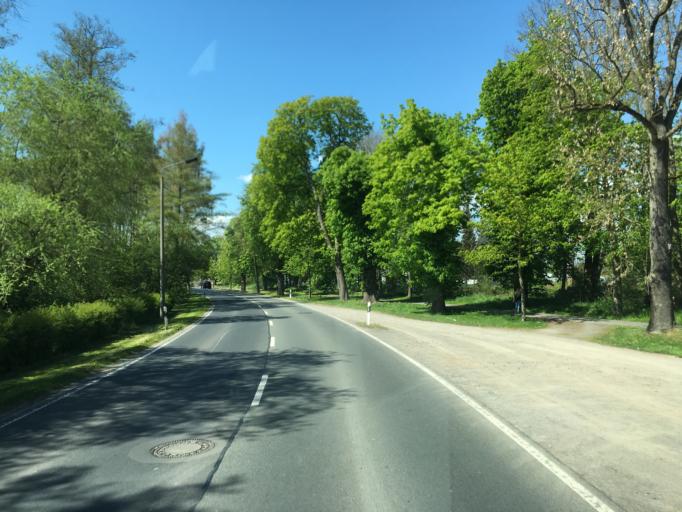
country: DE
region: Thuringia
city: Nordhausen
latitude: 51.5187
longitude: 10.7835
